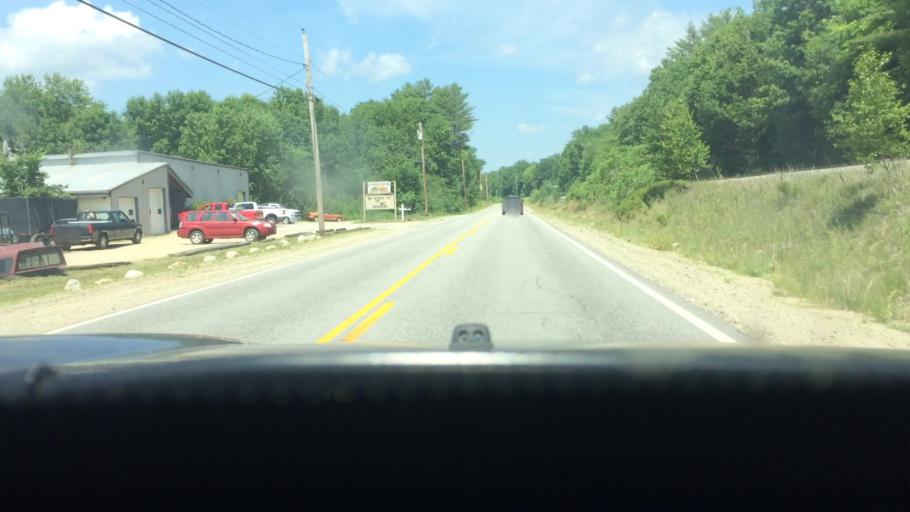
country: US
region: Maine
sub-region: Androscoggin County
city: Mechanic Falls
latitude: 44.1264
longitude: -70.4345
